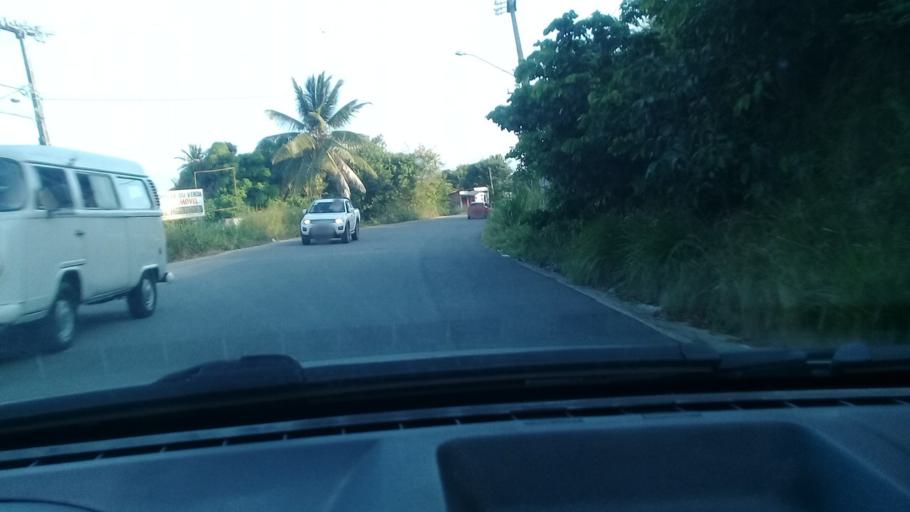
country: BR
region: Pernambuco
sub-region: Itamaraca
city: Itamaraca
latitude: -7.7770
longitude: -34.8356
